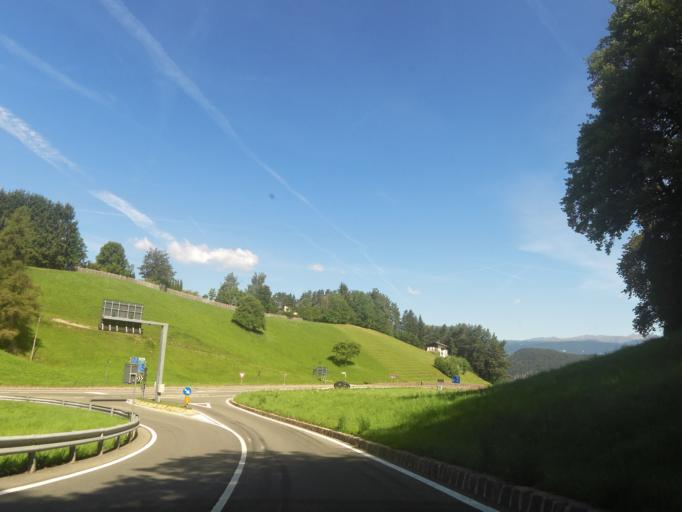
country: IT
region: Trentino-Alto Adige
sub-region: Bolzano
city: Castelrotto
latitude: 46.5545
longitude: 11.5580
